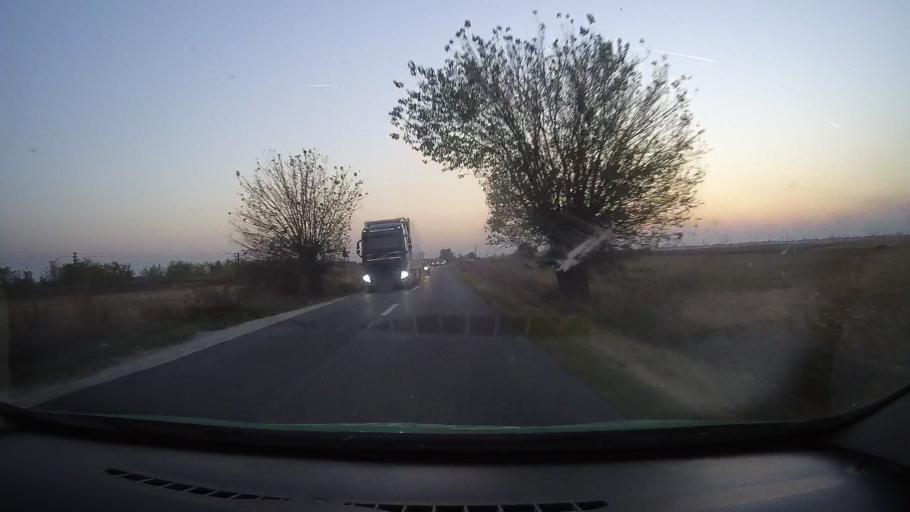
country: RO
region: Arad
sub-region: Comuna Zimandu Nou
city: Zimandu Nou
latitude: 46.2899
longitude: 21.4129
